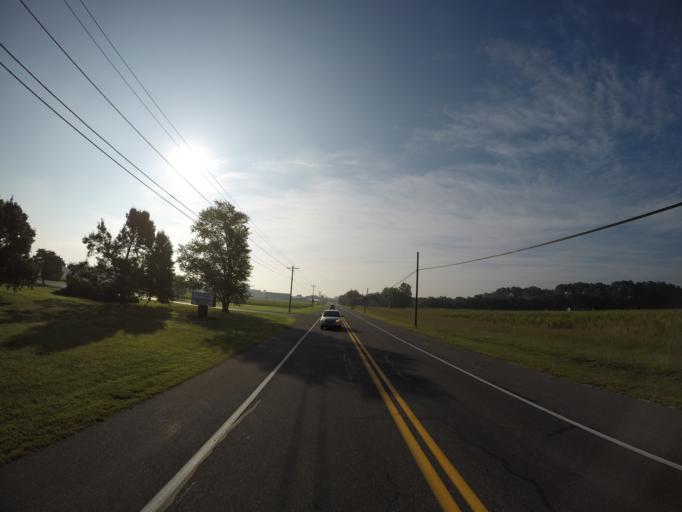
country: US
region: Delaware
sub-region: Sussex County
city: Millsboro
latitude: 38.5473
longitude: -75.2359
